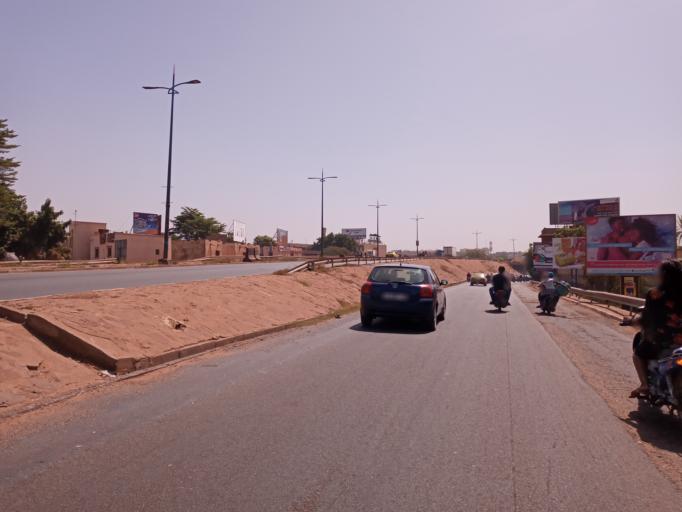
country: ML
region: Bamako
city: Bamako
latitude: 12.6156
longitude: -7.9996
